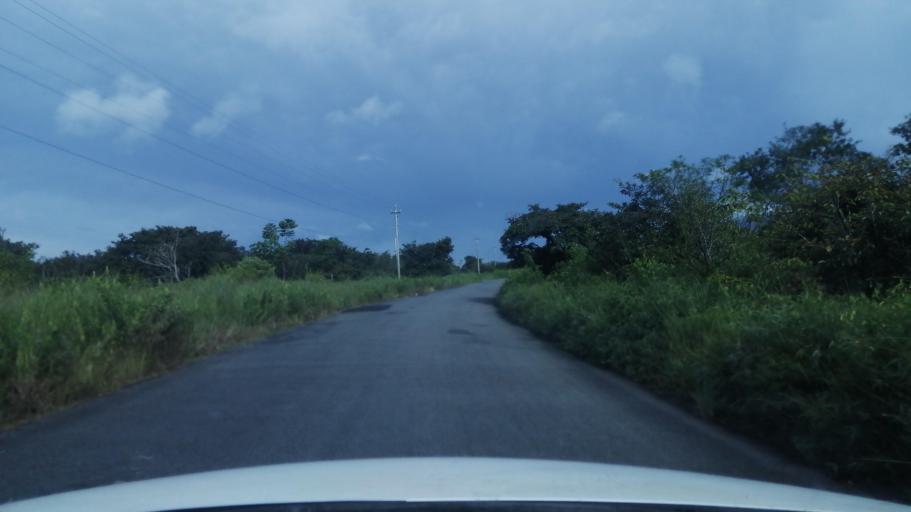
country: PA
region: Chiriqui
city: Potrerillos Abajo
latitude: 8.6678
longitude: -82.4297
